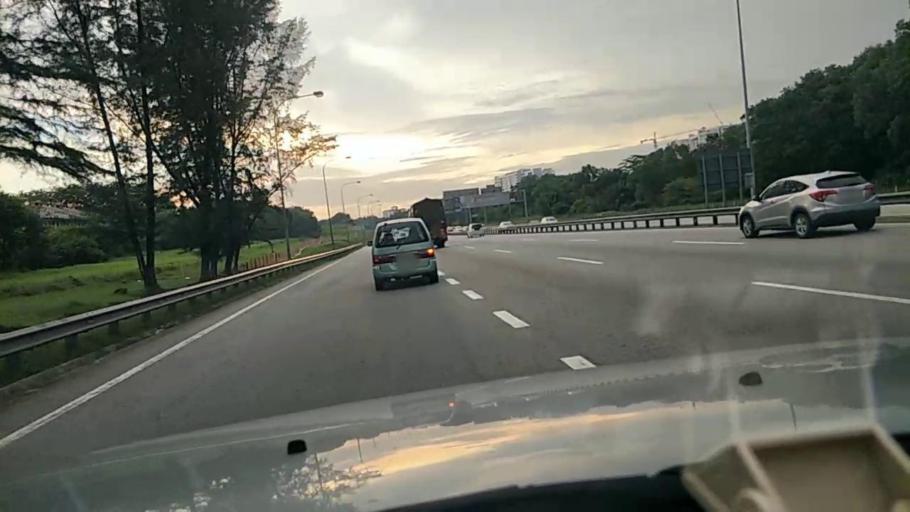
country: MY
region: Selangor
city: Shah Alam
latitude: 3.0931
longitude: 101.5447
